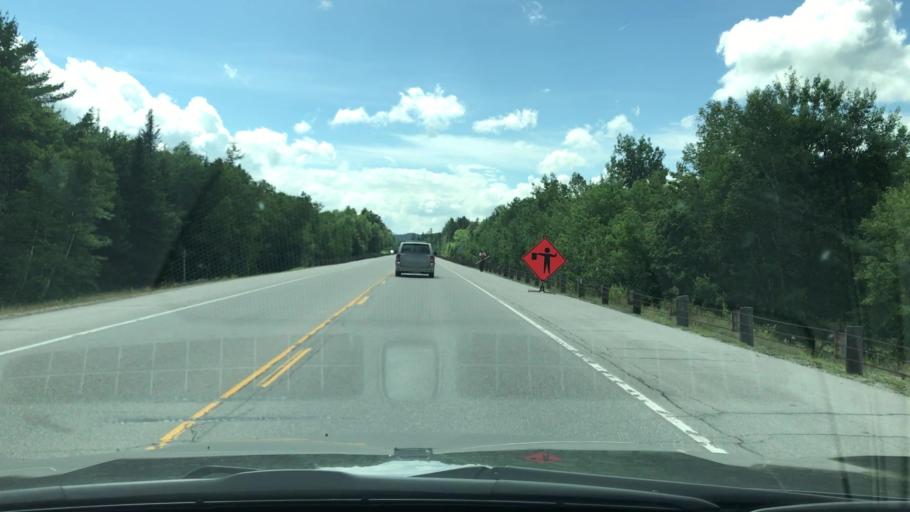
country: US
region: New Hampshire
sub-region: Coos County
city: Gorham
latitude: 44.3715
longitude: -71.2924
